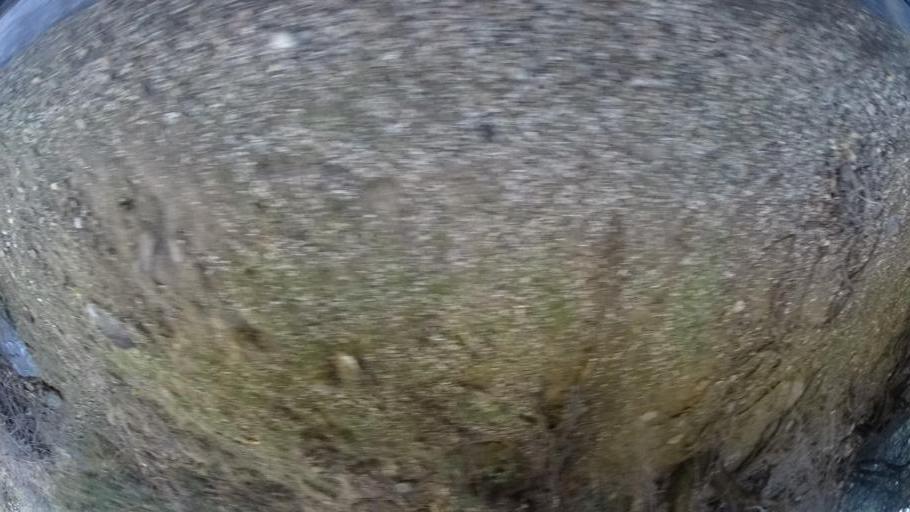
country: US
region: California
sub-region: Kern County
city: Golden Hills
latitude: 35.3086
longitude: -118.4988
